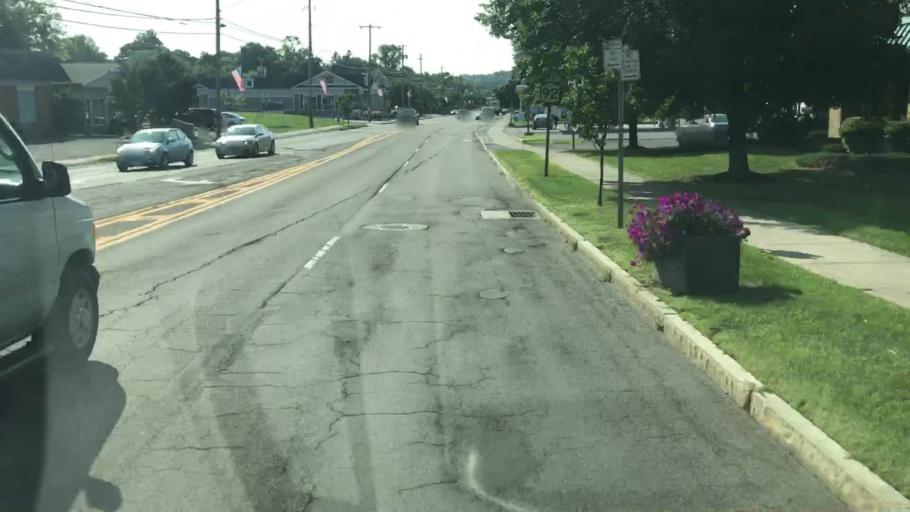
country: US
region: New York
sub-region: Onondaga County
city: Manlius
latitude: 43.0057
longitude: -75.9843
